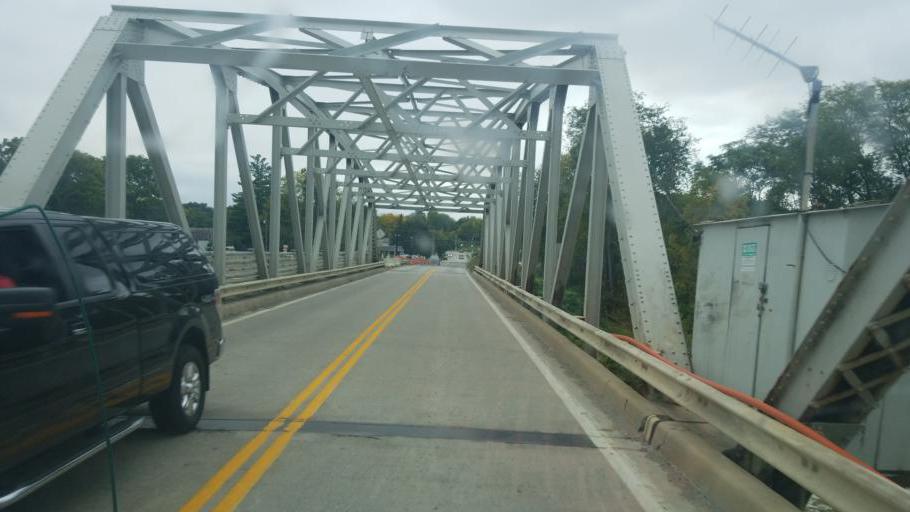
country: US
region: Ohio
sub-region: Lucas County
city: Waterville
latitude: 41.5003
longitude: -83.7145
